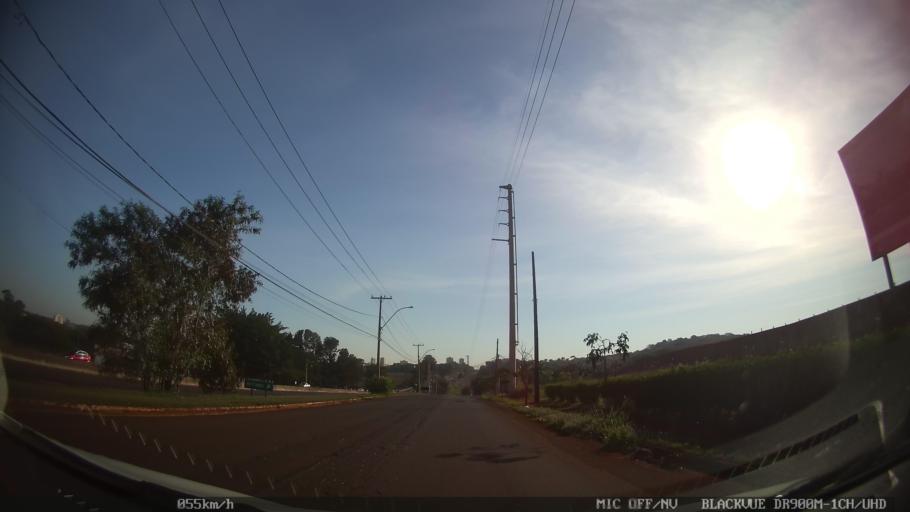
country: BR
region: Sao Paulo
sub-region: Ribeirao Preto
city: Ribeirao Preto
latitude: -21.2402
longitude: -47.8188
